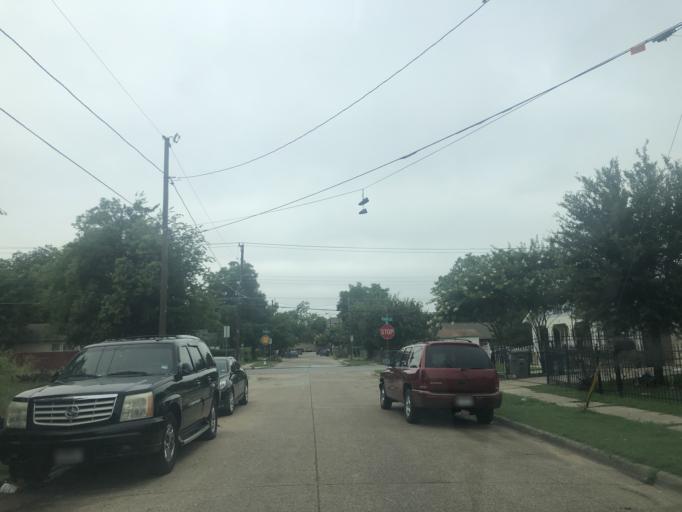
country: US
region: Texas
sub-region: Dallas County
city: Dallas
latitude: 32.7802
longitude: -96.8529
